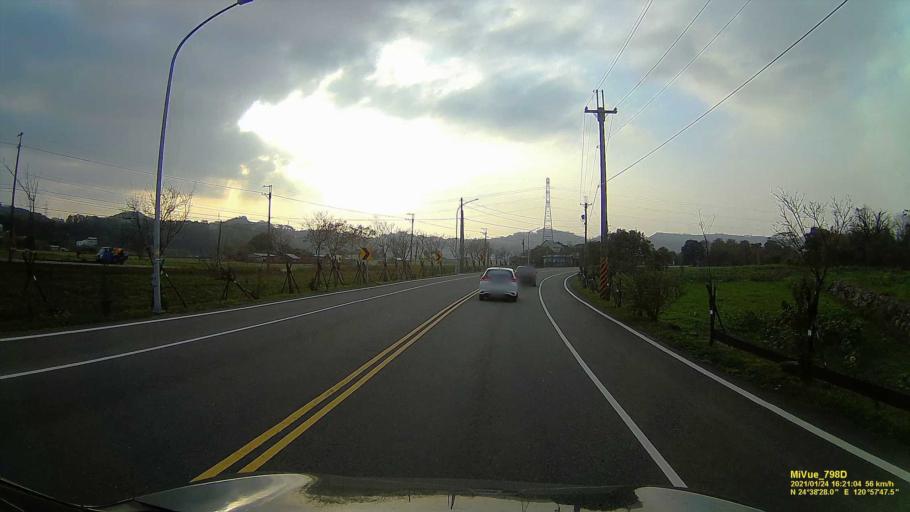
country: TW
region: Taiwan
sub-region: Miaoli
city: Miaoli
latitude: 24.6410
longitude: 120.9632
